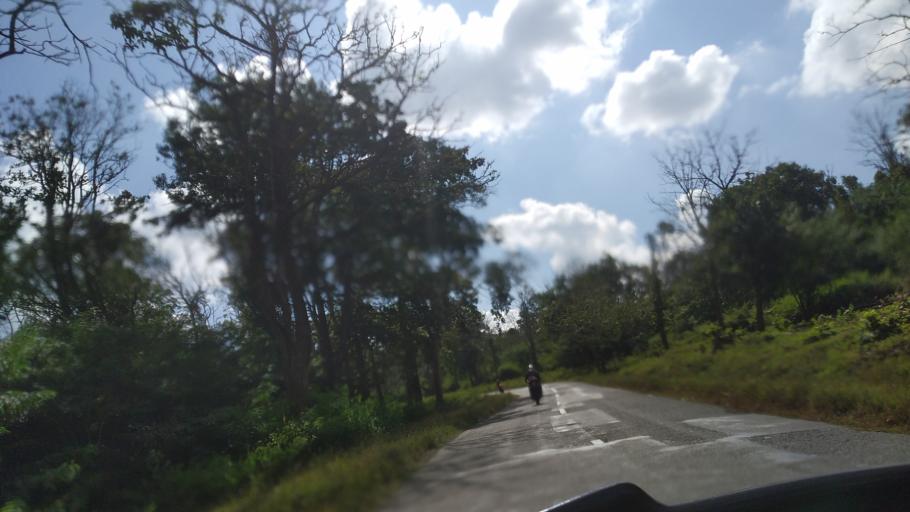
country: IN
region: Kerala
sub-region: Wayanad
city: Panamaram
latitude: 11.9300
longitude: 76.0664
